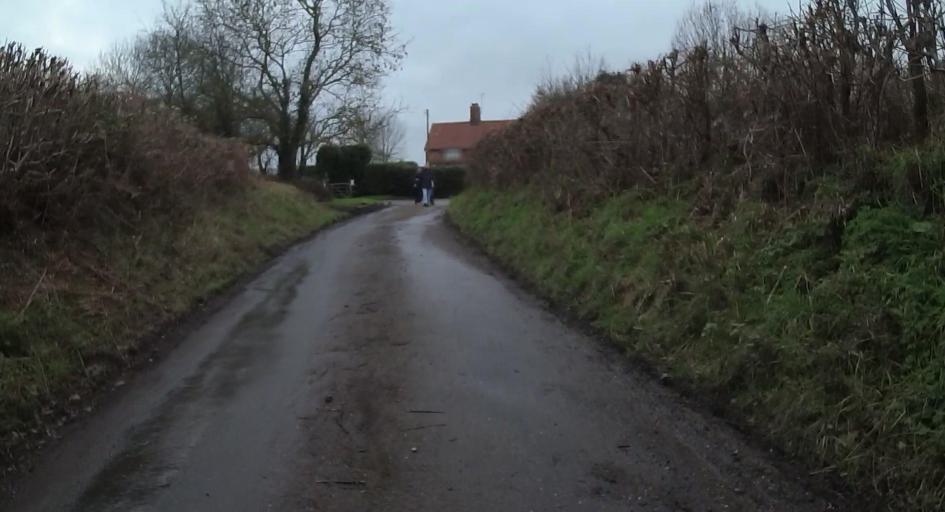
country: GB
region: England
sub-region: West Berkshire
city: Stratfield Mortimer
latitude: 51.3797
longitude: -1.0448
